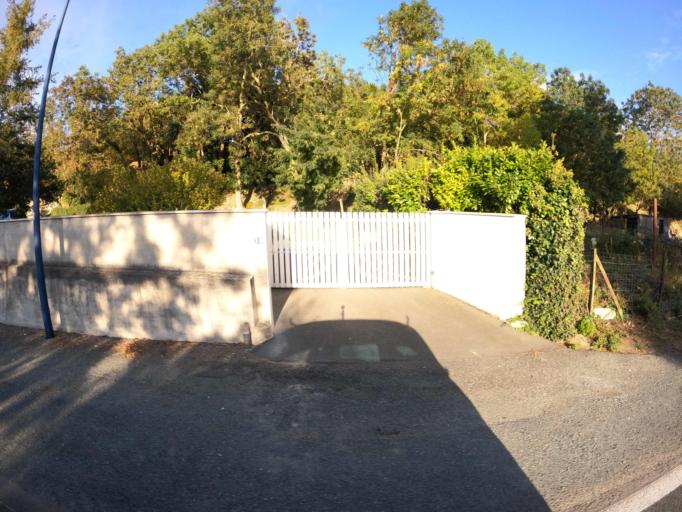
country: FR
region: Pays de la Loire
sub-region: Departement de la Vendee
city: Chaille-les-Marais
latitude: 46.4031
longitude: -1.0345
